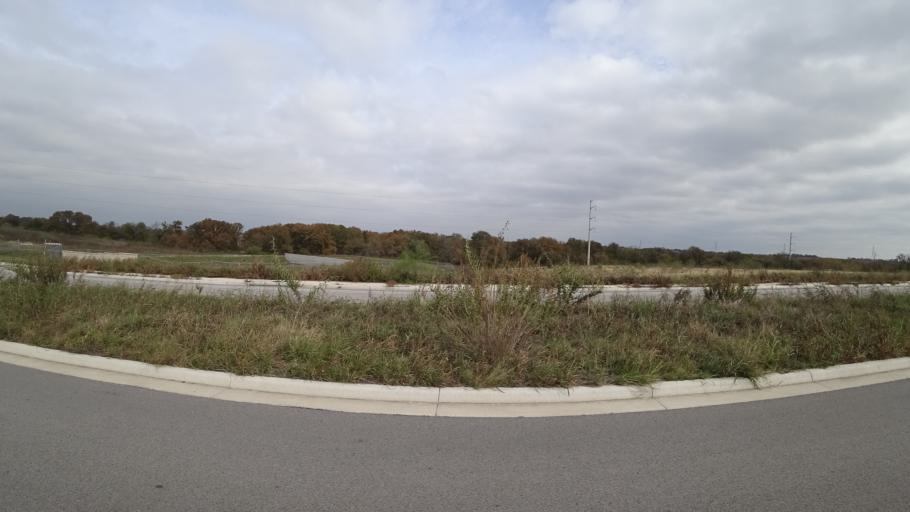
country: US
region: Texas
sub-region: Travis County
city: Manor
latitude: 30.3738
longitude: -97.5949
